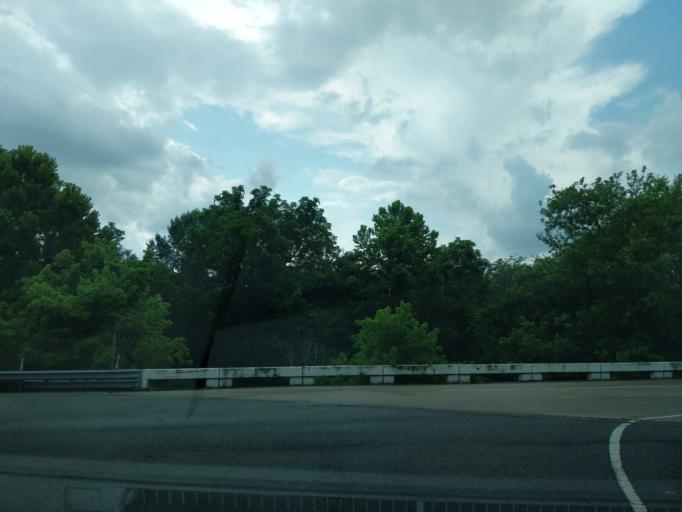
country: US
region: Tennessee
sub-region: Davidson County
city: Belle Meade
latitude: 36.0443
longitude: -86.9500
